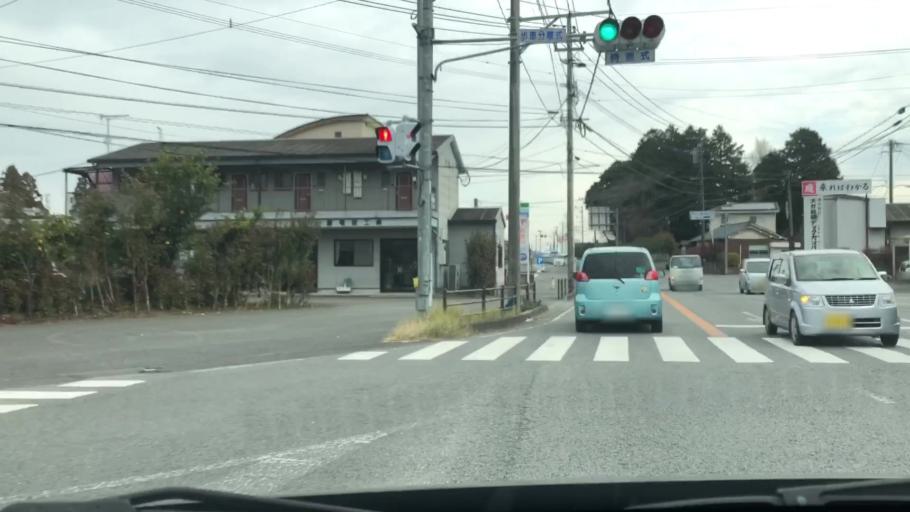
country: JP
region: Oita
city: Takedamachi
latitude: 32.9921
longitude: 131.6120
